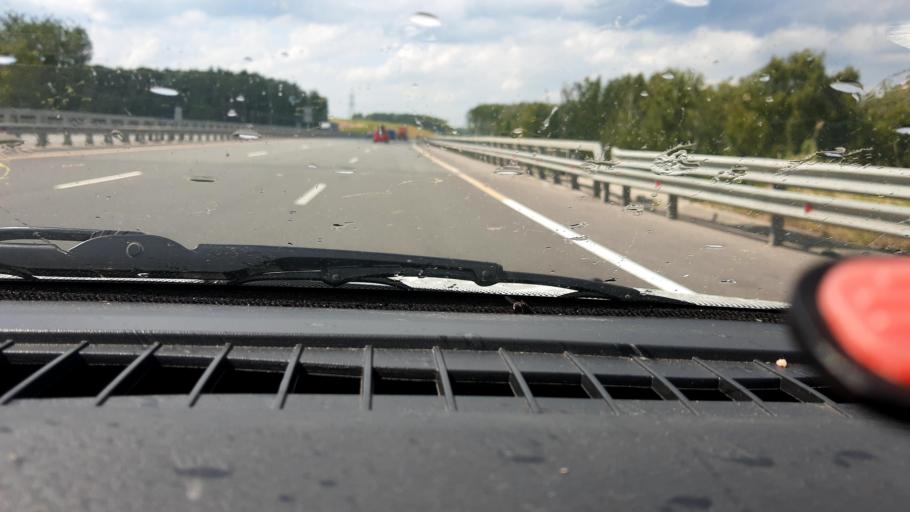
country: RU
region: Nizjnij Novgorod
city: Kstovo
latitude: 56.0667
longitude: 44.1207
